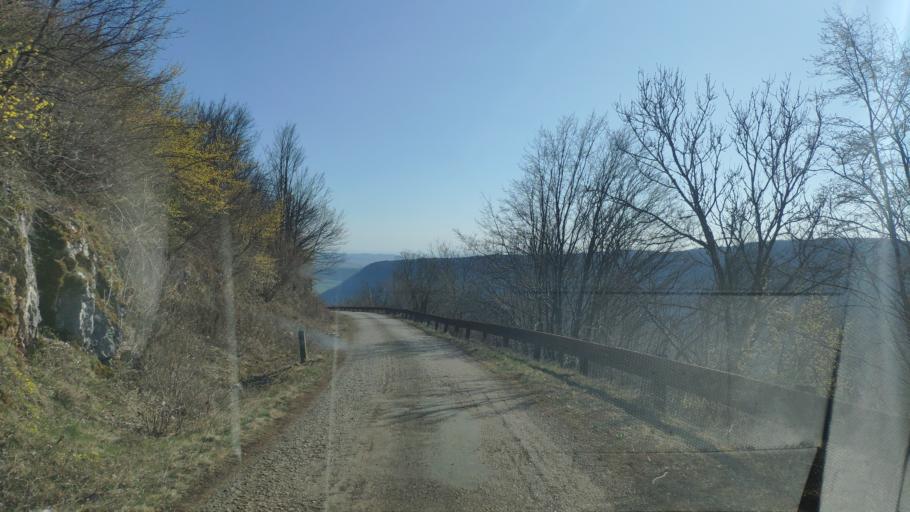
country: SK
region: Kosicky
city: Roznava
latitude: 48.5822
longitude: 20.4039
